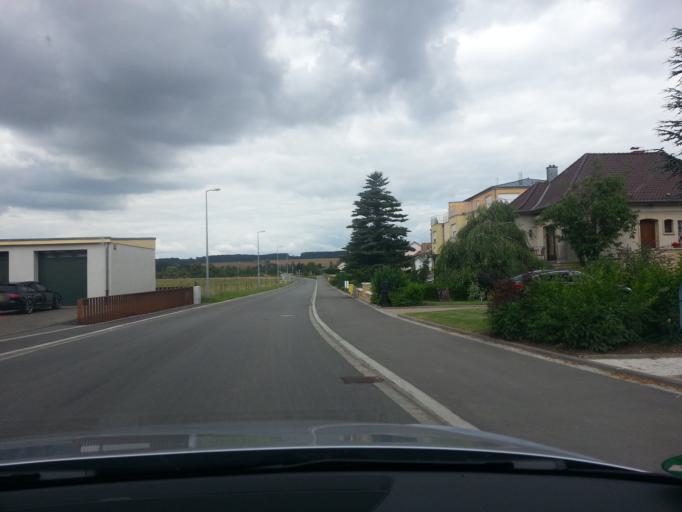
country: LU
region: Grevenmacher
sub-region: Canton de Remich
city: Mondorf-les-Bains
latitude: 49.5163
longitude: 6.3041
